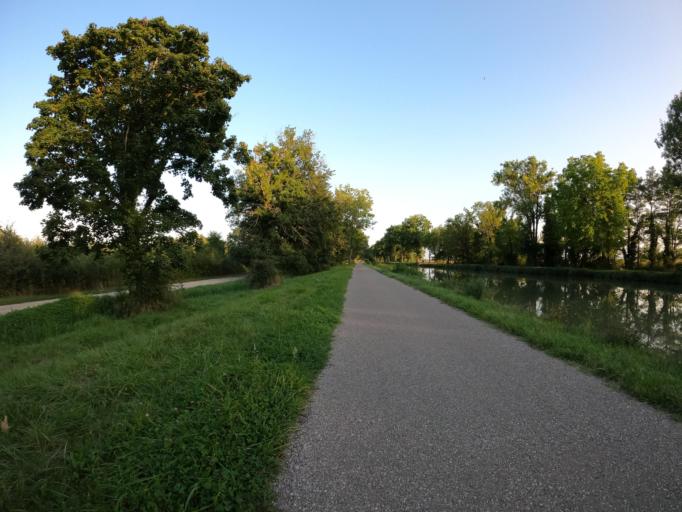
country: FR
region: Midi-Pyrenees
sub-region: Departement du Tarn-et-Garonne
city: Saint-Porquier
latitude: 43.9862
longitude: 1.2078
